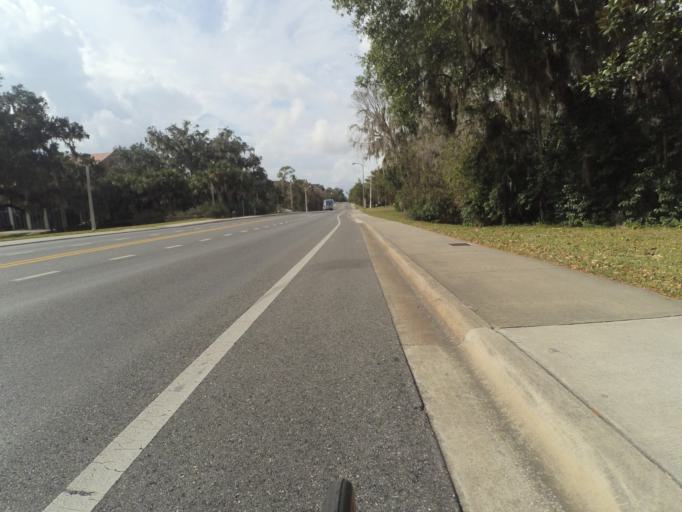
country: US
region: Florida
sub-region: Alachua County
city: Gainesville
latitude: 29.6449
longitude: -82.3491
